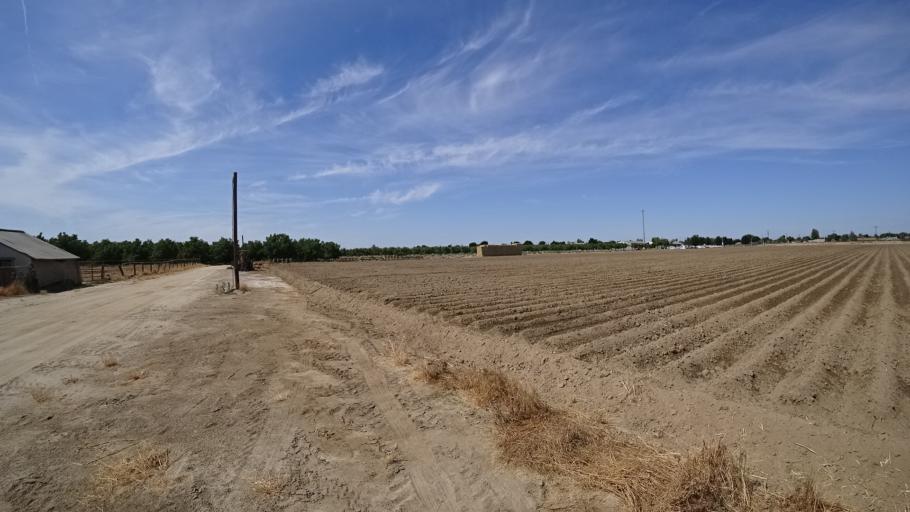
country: US
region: California
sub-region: Kings County
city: Hanford
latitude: 36.3507
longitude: -119.6223
